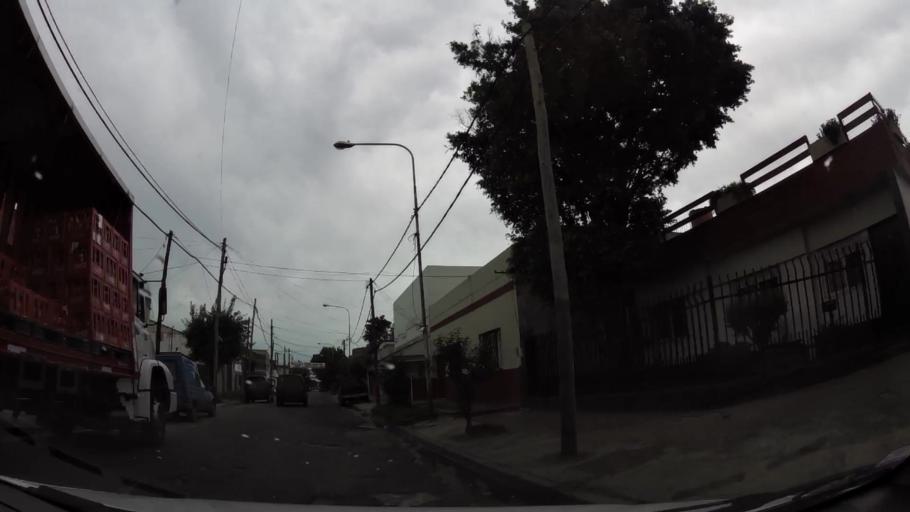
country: AR
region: Buenos Aires
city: San Justo
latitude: -34.6708
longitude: -58.5219
